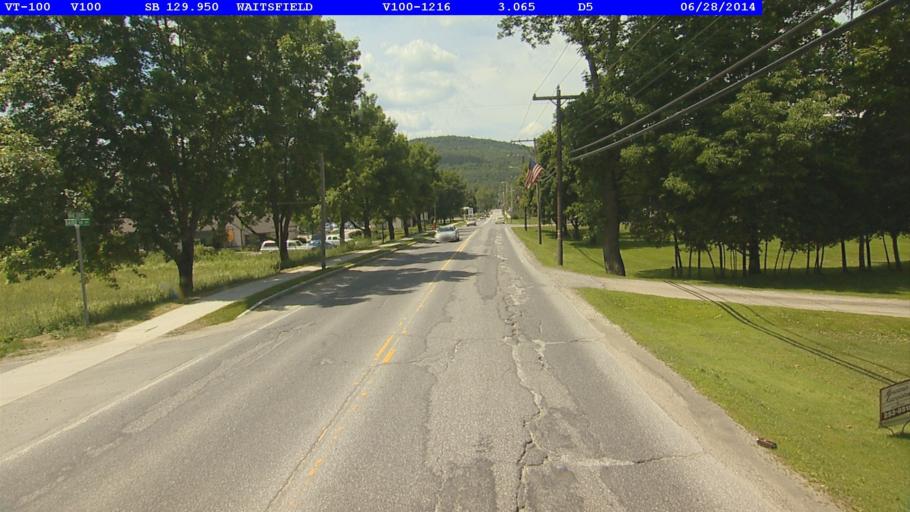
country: US
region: Vermont
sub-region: Washington County
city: Waterbury
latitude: 44.1860
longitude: -72.8342
